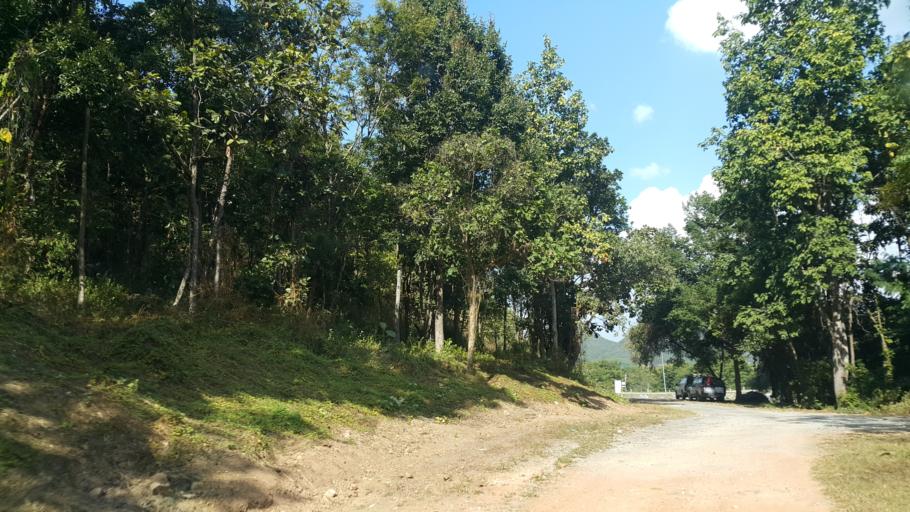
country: TH
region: Lamphun
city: Ban Thi
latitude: 18.5839
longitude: 99.1520
